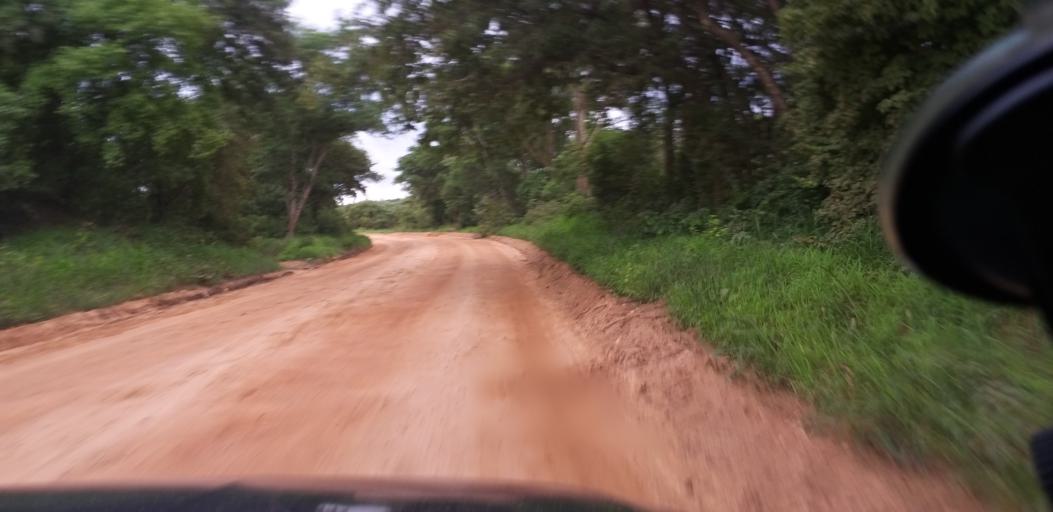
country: ZM
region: Lusaka
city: Lusaka
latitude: -15.1875
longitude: 28.4461
